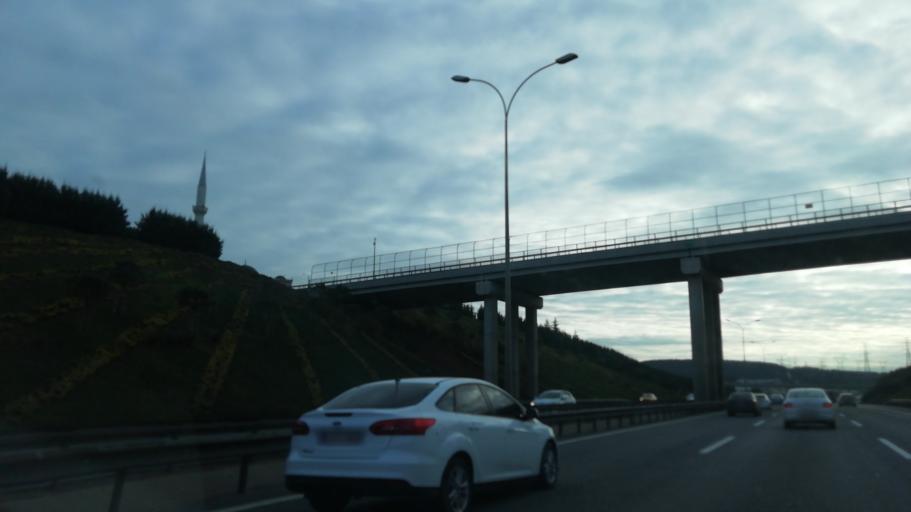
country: TR
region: Istanbul
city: Sultanbeyli
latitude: 40.9526
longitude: 29.2997
